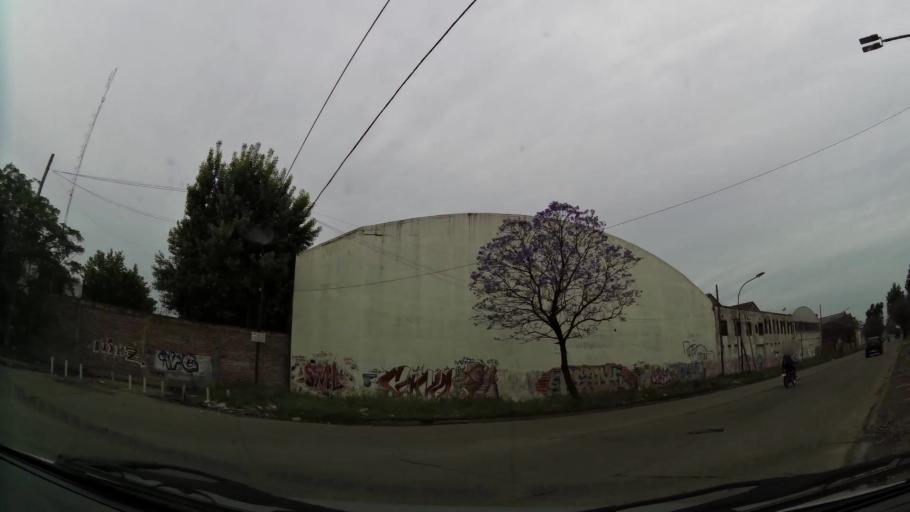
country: AR
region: Buenos Aires
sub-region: Partido de Lanus
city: Lanus
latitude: -34.7119
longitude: -58.3643
